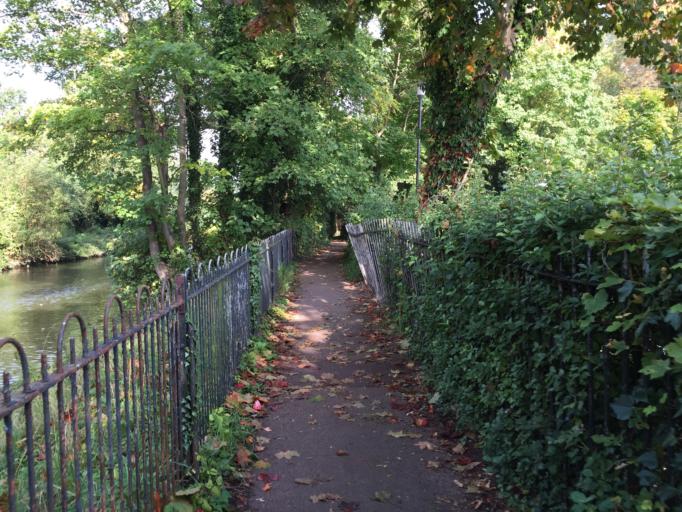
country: GB
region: England
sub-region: West Berkshire
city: Eton
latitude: 51.4882
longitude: -0.6051
